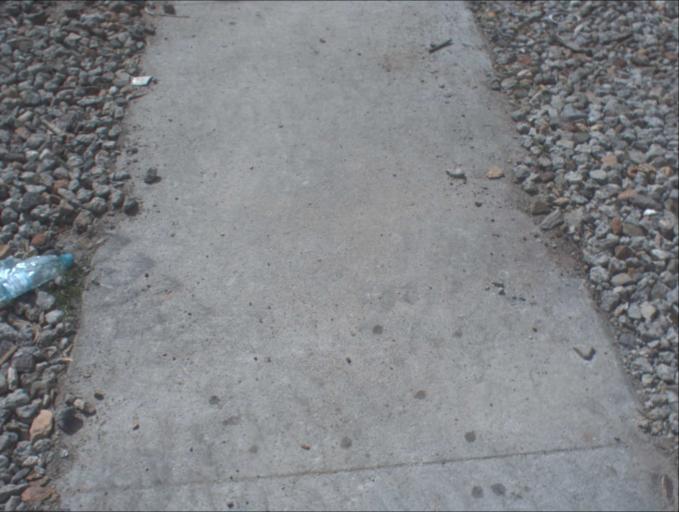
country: AU
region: Queensland
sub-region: Logan
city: Logan City
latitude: -27.6762
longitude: 153.0926
